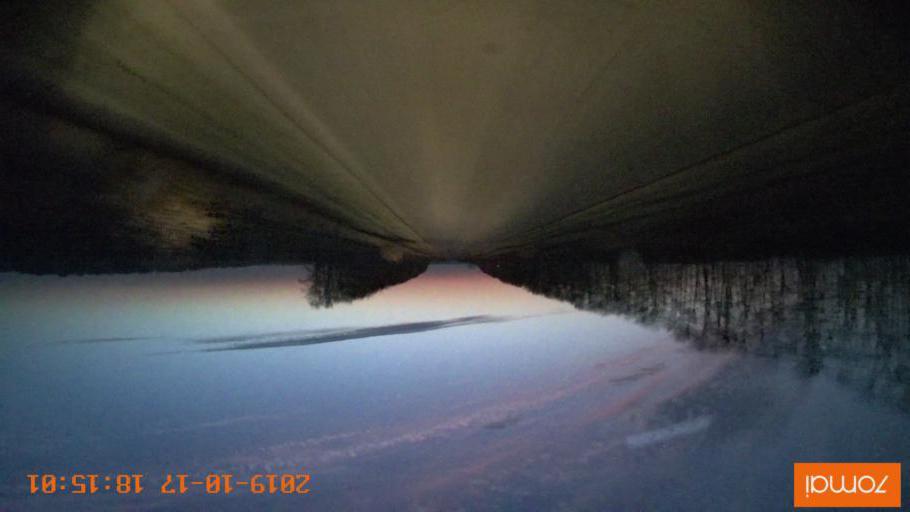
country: RU
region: Tula
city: Kurkino
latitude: 53.4054
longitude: 38.5477
